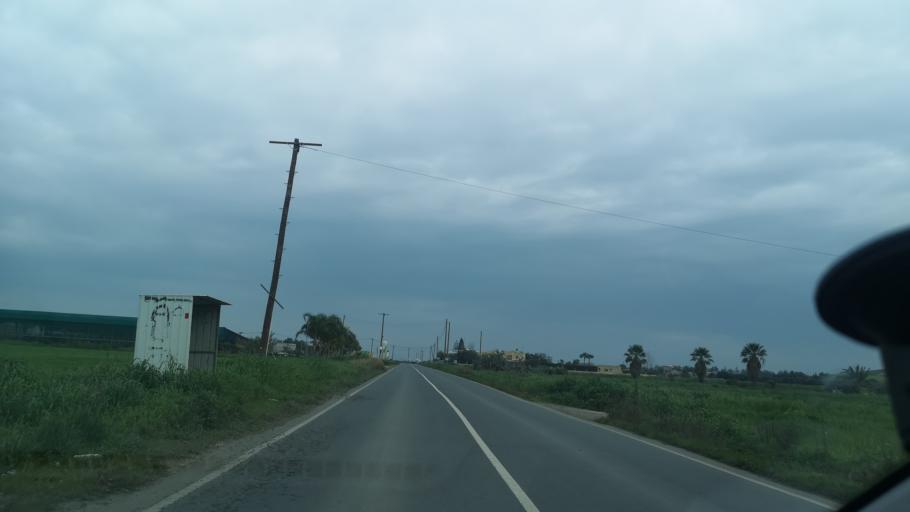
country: CY
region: Lefkosia
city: Tseri
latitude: 35.0813
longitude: 33.3023
